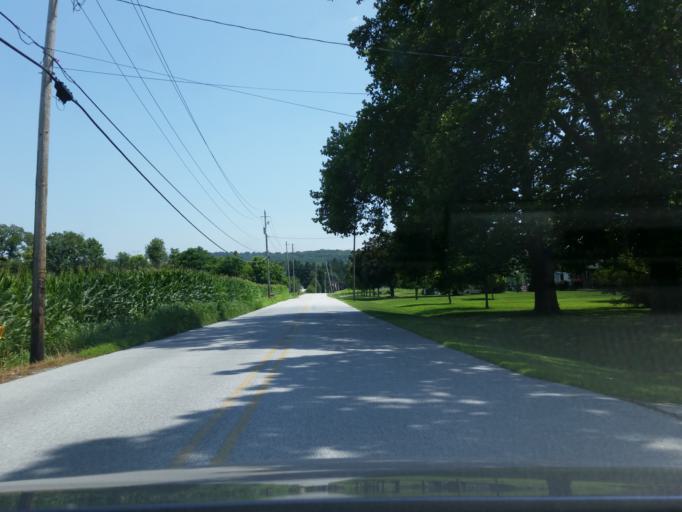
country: US
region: Pennsylvania
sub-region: York County
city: Stonybrook
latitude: 39.9929
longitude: -76.6284
